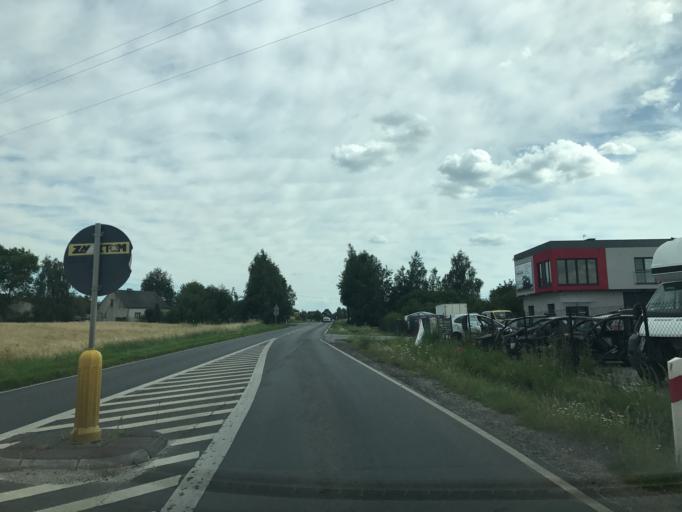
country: PL
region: Kujawsko-Pomorskie
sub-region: Powiat brodnicki
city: Brodnica
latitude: 53.2212
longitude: 19.3854
